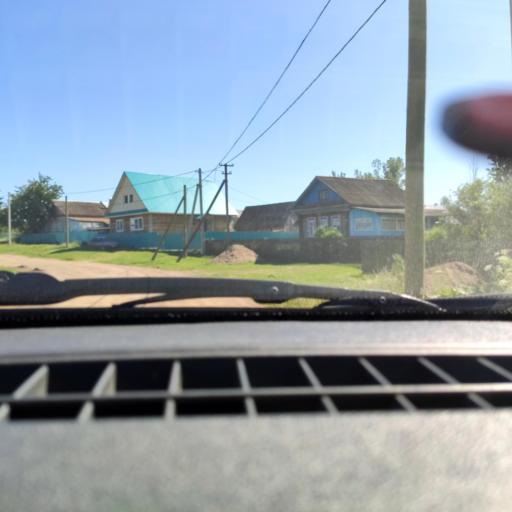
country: RU
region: Bashkortostan
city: Iglino
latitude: 54.8964
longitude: 56.4933
